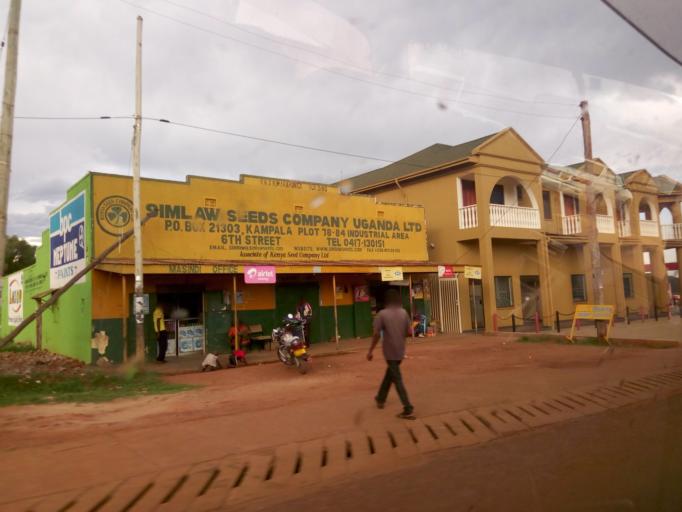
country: UG
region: Western Region
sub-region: Masindi District
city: Masindi
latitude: 1.6841
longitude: 31.7206
